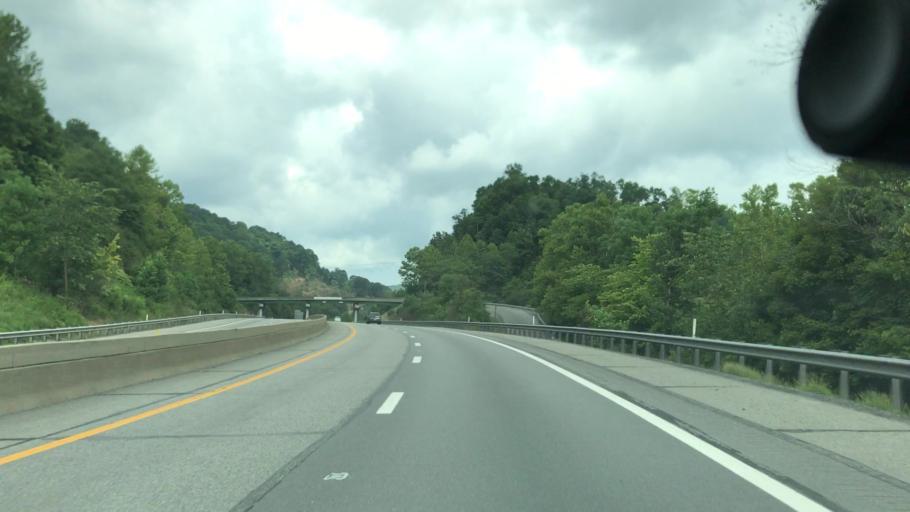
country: US
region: West Virginia
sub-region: Fayette County
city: Oak Hill
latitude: 37.9792
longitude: -81.2965
